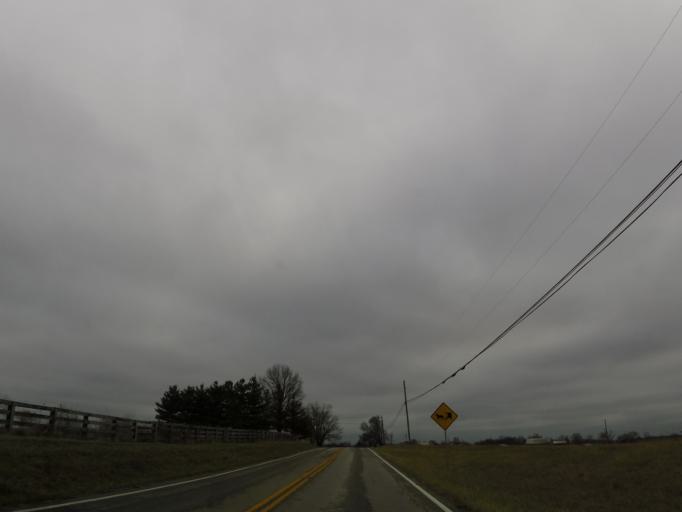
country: US
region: Kentucky
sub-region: Henry County
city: Eminence
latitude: 38.3488
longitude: -85.0634
